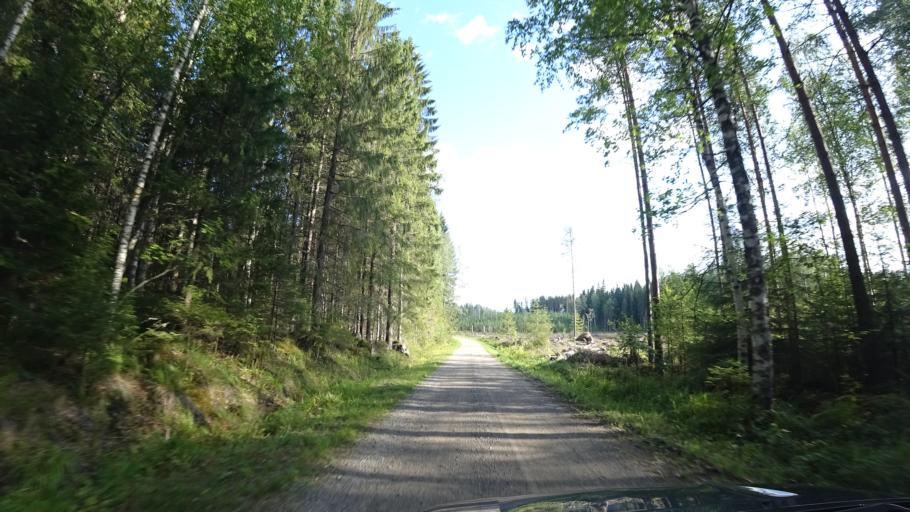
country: FI
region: Paijanne Tavastia
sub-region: Lahti
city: Auttoinen
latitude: 61.2178
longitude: 25.1510
